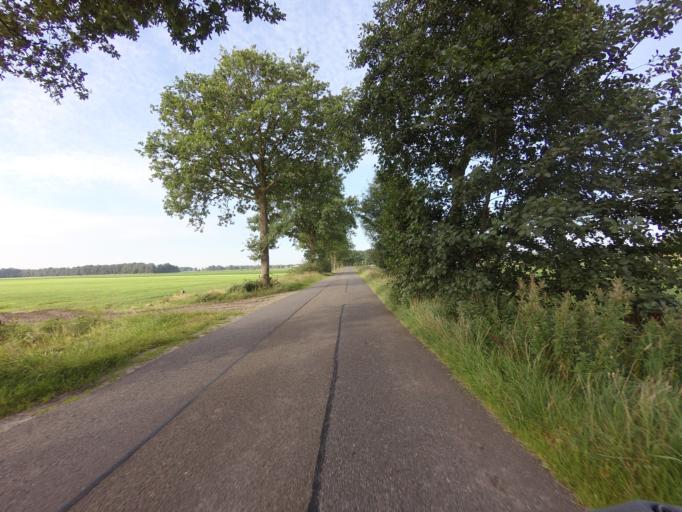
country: NL
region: Friesland
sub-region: Gemeente Weststellingwerf
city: Noordwolde
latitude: 52.9323
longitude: 6.1940
